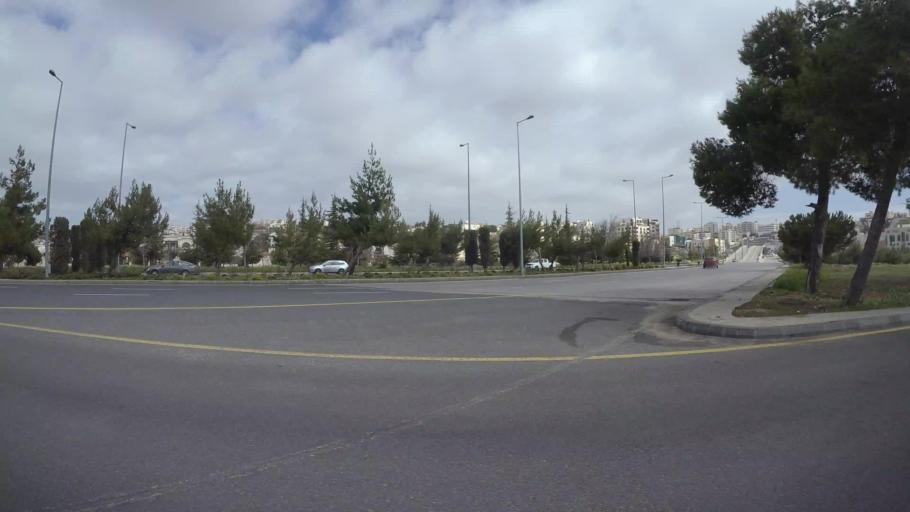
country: JO
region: Amman
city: Wadi as Sir
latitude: 31.9924
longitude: 35.8267
